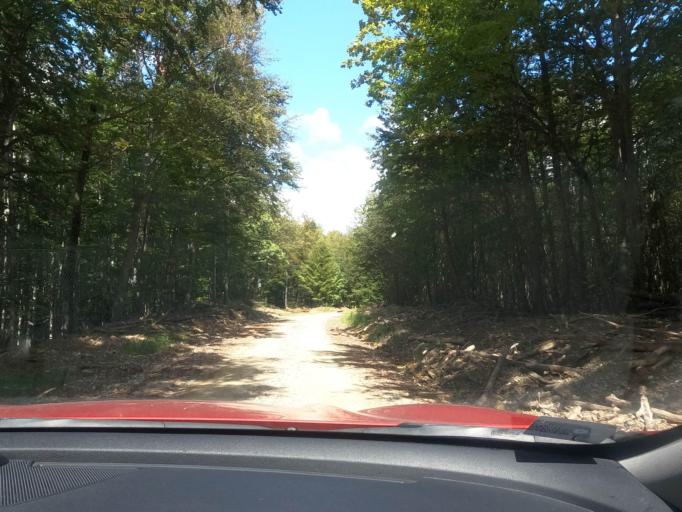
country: BA
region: Federation of Bosnia and Herzegovina
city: Velika Kladusa
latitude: 45.2721
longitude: 15.7777
